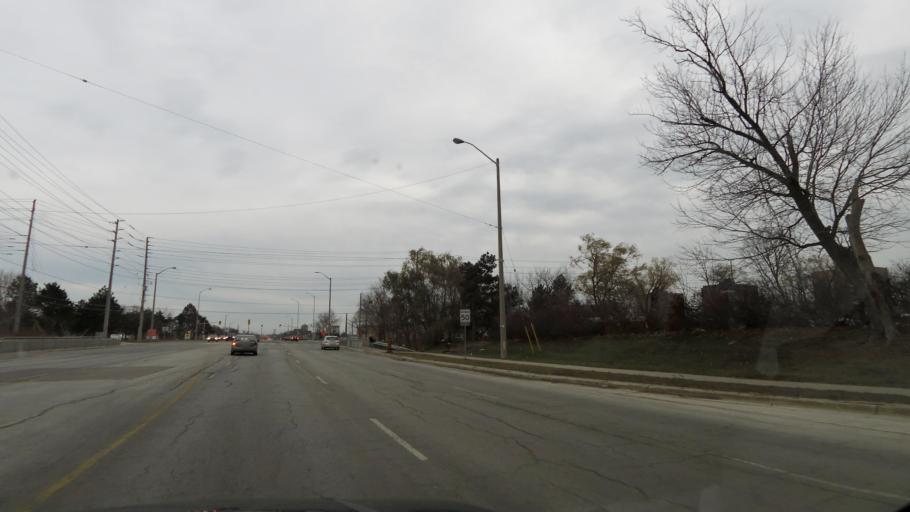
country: CA
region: Ontario
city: Etobicoke
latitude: 43.6123
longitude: -79.5881
